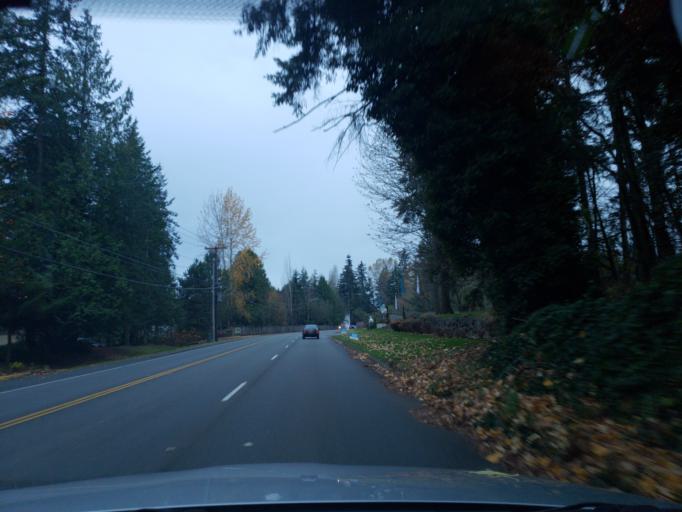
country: US
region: Washington
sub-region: King County
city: Inglewood-Finn Hill
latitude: 47.7333
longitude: -122.2162
